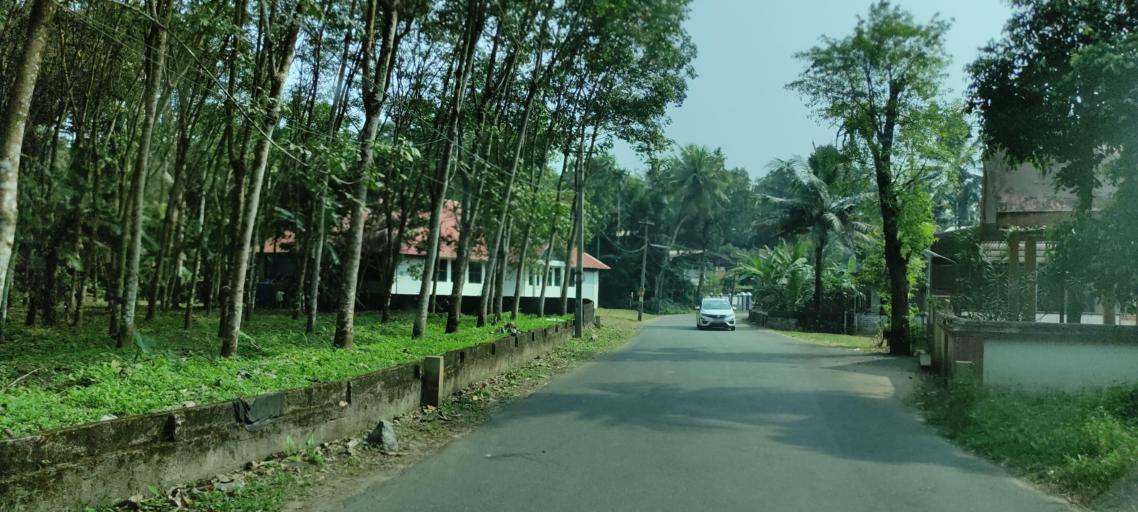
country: IN
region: Kerala
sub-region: Pattanamtitta
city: Adur
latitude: 9.2270
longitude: 76.7128
